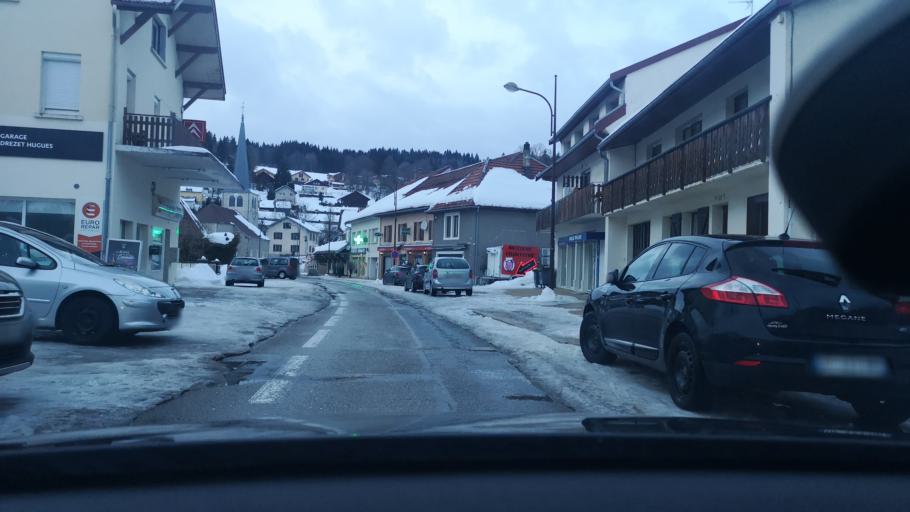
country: FR
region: Franche-Comte
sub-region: Departement du Doubs
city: Jougne
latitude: 46.7768
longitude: 6.3749
